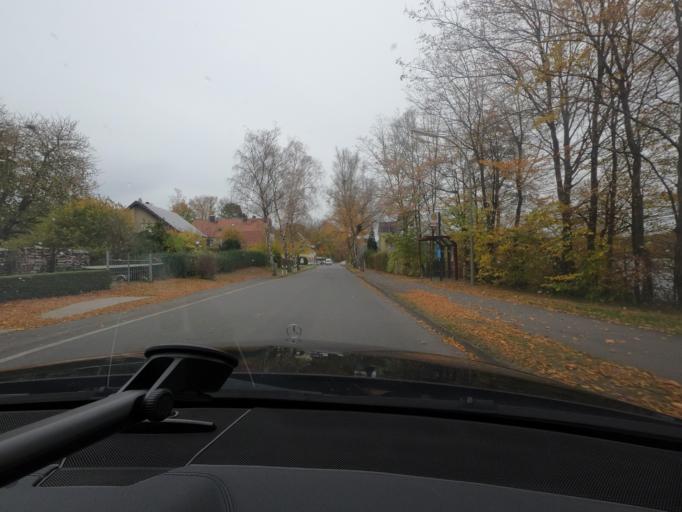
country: DE
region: North Rhine-Westphalia
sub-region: Regierungsbezirk Arnsberg
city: Mohnesee
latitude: 51.4877
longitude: 8.1714
